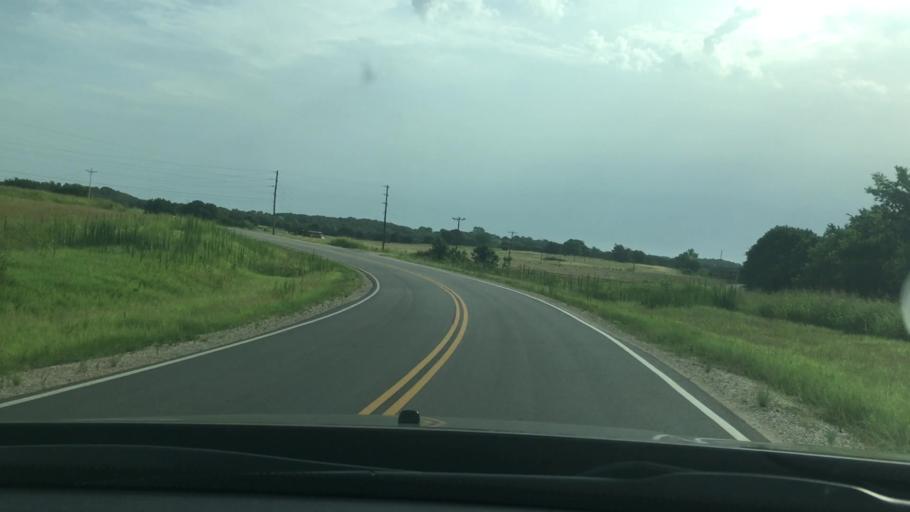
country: US
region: Oklahoma
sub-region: Pontotoc County
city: Byng
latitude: 34.8528
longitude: -96.6143
